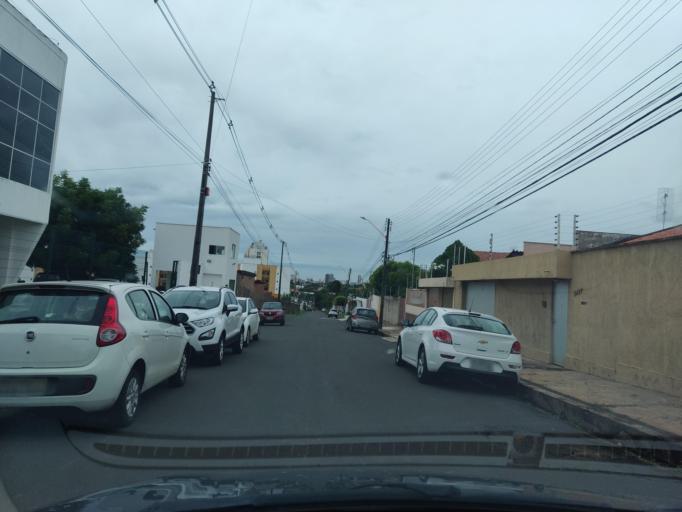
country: BR
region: Piaui
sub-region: Teresina
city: Teresina
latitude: -5.0760
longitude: -42.7522
